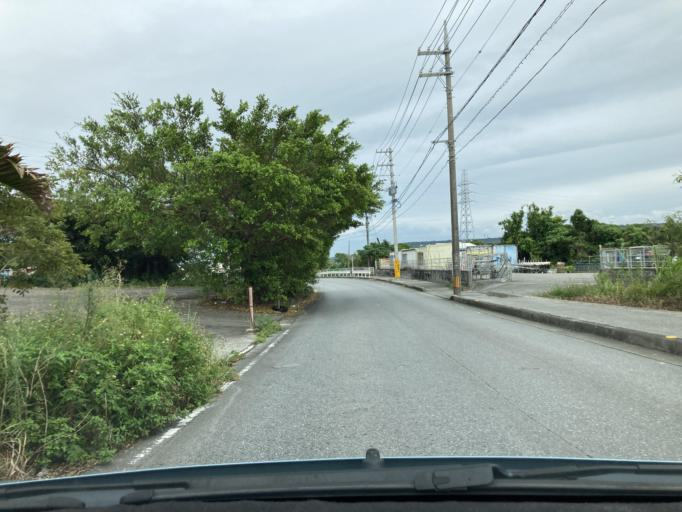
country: JP
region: Okinawa
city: Itoman
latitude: 26.1429
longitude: 127.6819
